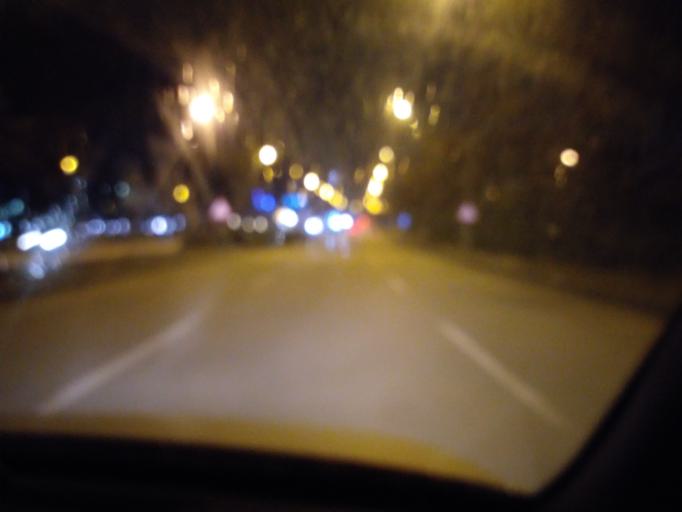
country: TR
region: Ankara
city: Batikent
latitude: 39.8823
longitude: 32.7125
